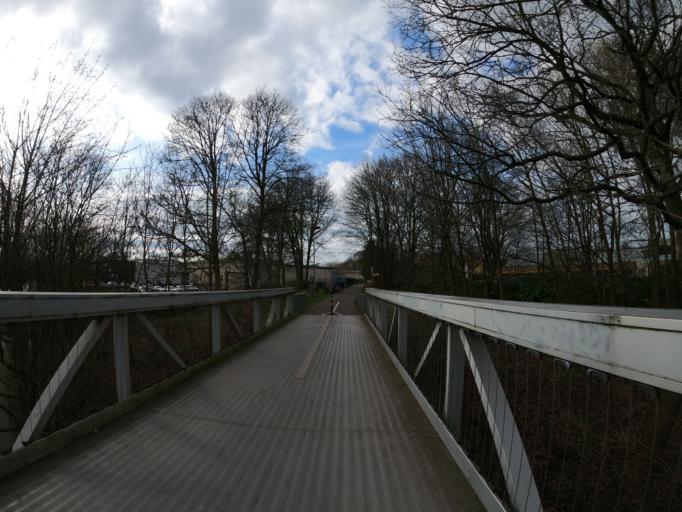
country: DE
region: North Rhine-Westphalia
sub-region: Regierungsbezirk Dusseldorf
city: Solingen
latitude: 51.1861
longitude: 7.0563
